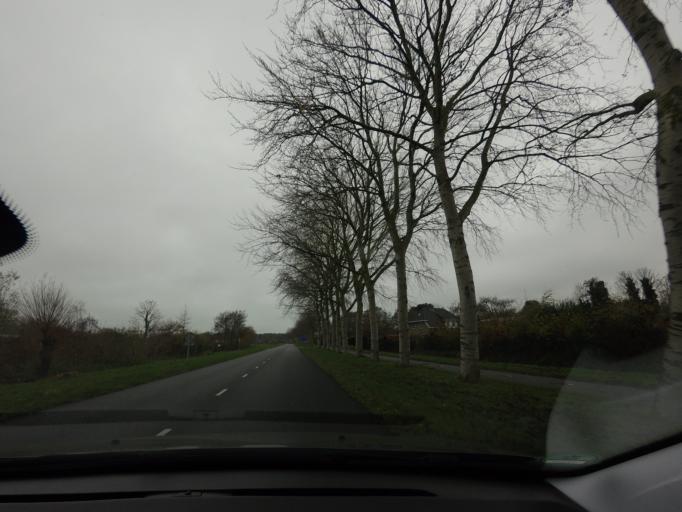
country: NL
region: Zeeland
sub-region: Schouwen-Duiveland
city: Burgh
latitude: 51.6781
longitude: 3.7182
